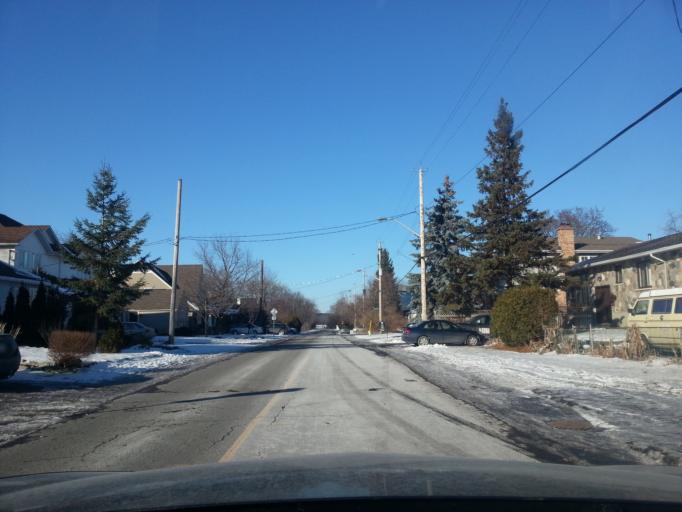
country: CA
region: Ontario
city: Ottawa
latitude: 45.3970
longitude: -75.7570
